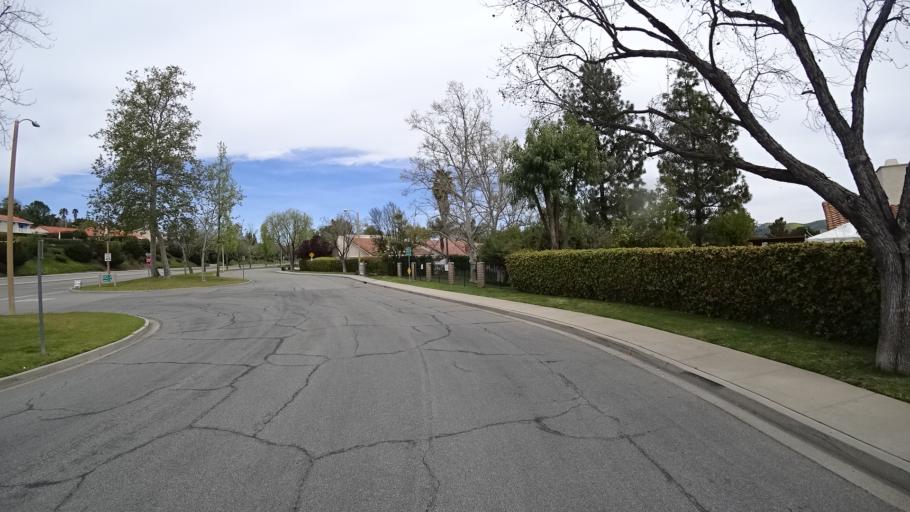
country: US
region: California
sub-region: Los Angeles County
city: Westlake Village
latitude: 34.1418
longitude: -118.8340
